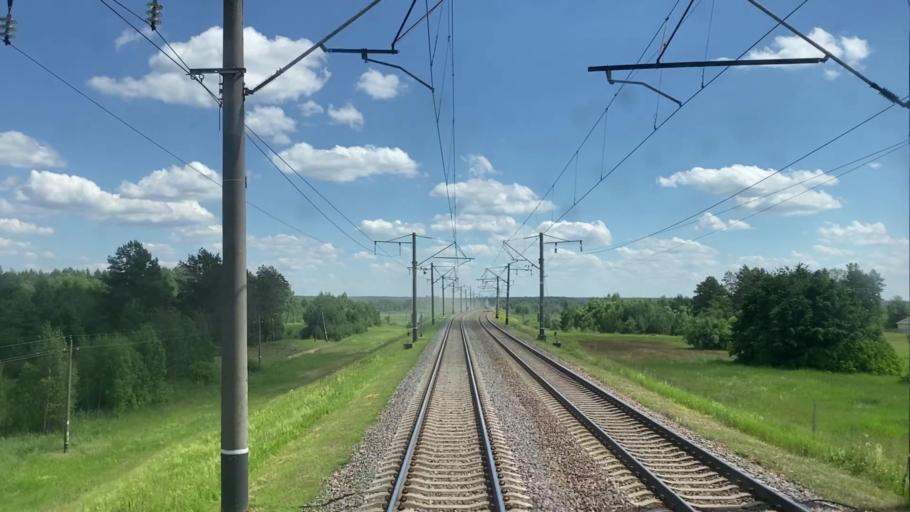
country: BY
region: Brest
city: Ivatsevichy
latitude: 52.8392
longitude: 25.5304
